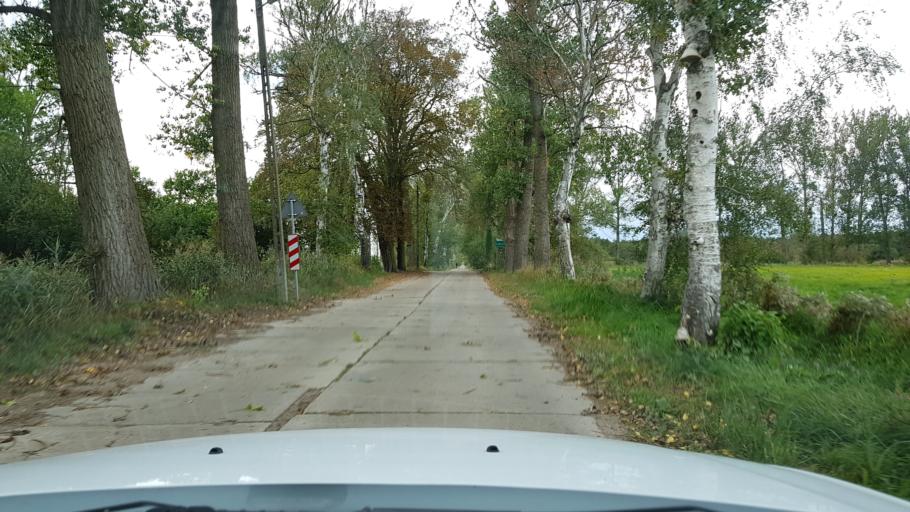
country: PL
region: West Pomeranian Voivodeship
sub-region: Powiat gryfinski
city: Gryfino
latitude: 53.3194
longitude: 14.5312
